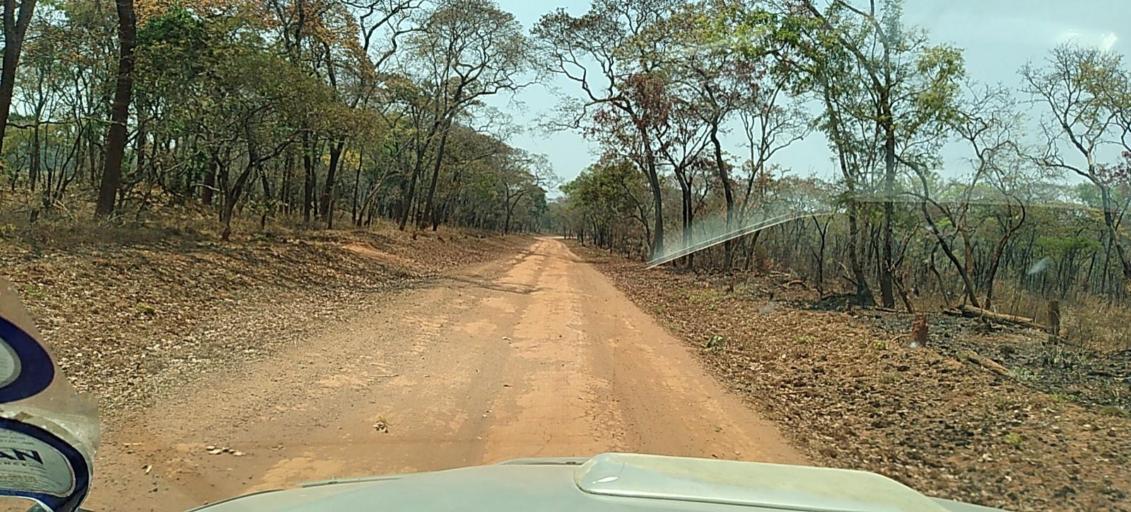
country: ZM
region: North-Western
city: Kasempa
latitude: -13.5483
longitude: 26.0570
